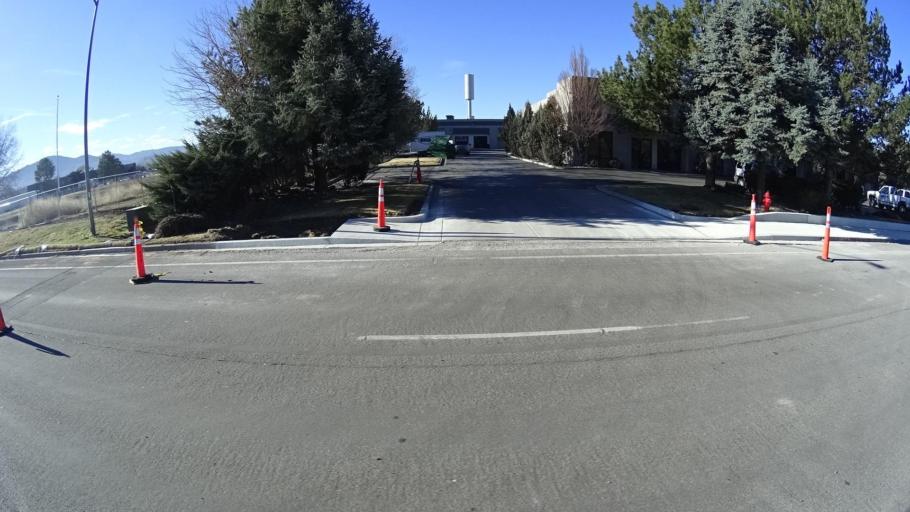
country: US
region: Nevada
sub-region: Washoe County
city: Sparks
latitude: 39.5143
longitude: -119.7537
